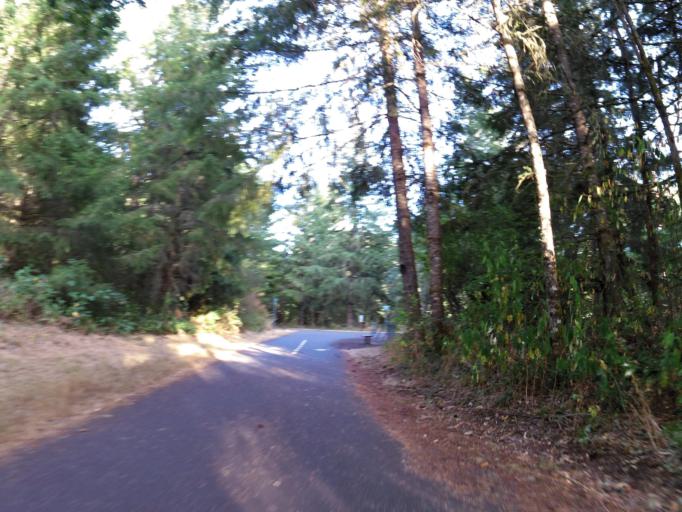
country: US
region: Washington
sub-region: Thurston County
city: Rainier
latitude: 46.8748
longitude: -122.7224
